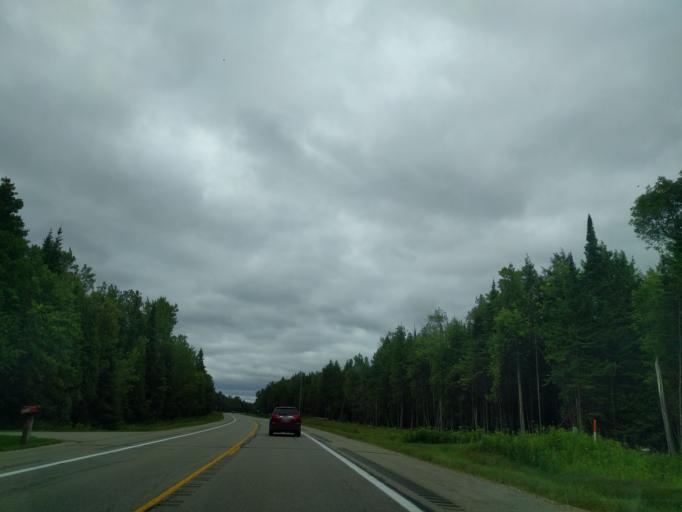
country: US
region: Michigan
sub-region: Delta County
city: Escanaba
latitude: 45.5915
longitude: -87.2367
